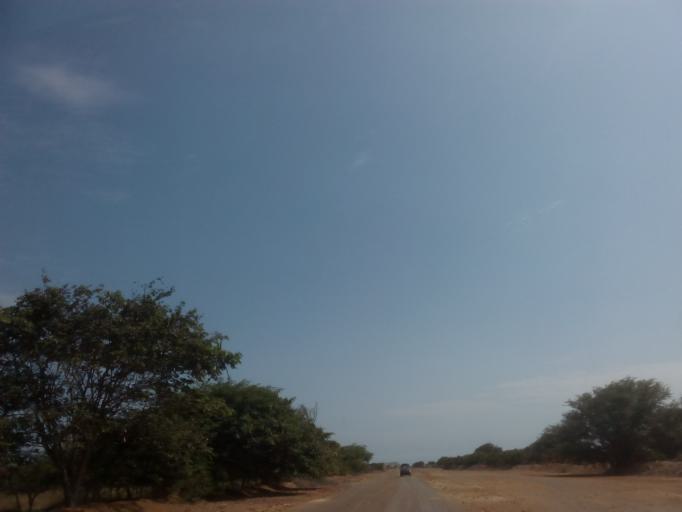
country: PE
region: La Libertad
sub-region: Chepen
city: Pueblo Nuevo
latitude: -7.1469
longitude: -79.6029
